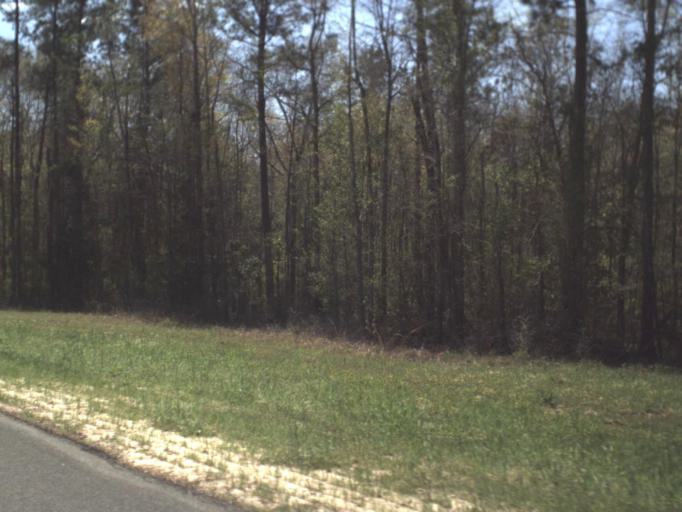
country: US
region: Florida
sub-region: Walton County
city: DeFuniak Springs
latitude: 30.7819
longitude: -85.9587
